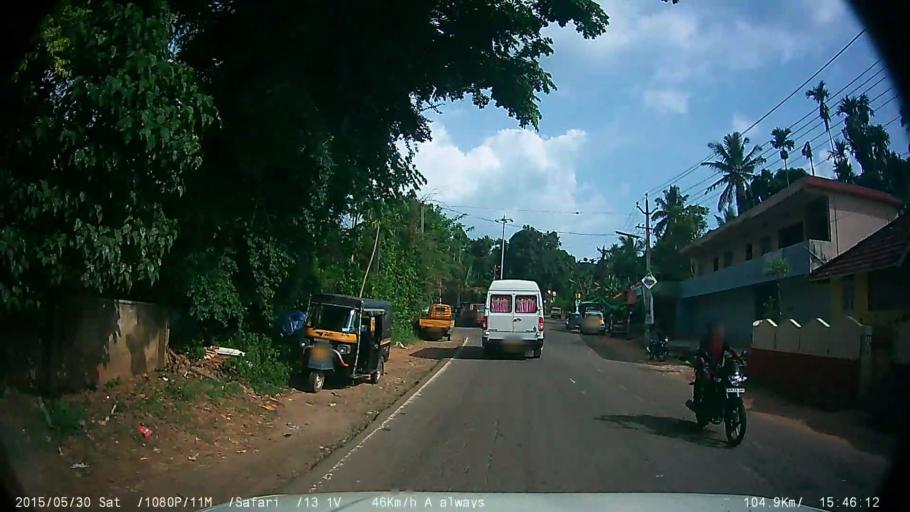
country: IN
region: Kerala
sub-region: Wayanad
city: Panamaram
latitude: 11.7119
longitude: 76.0794
